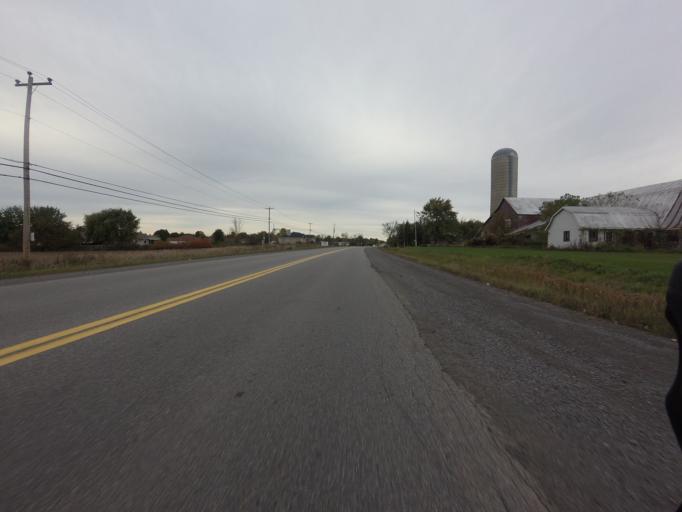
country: CA
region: Ontario
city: Bells Corners
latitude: 45.1397
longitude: -75.7146
